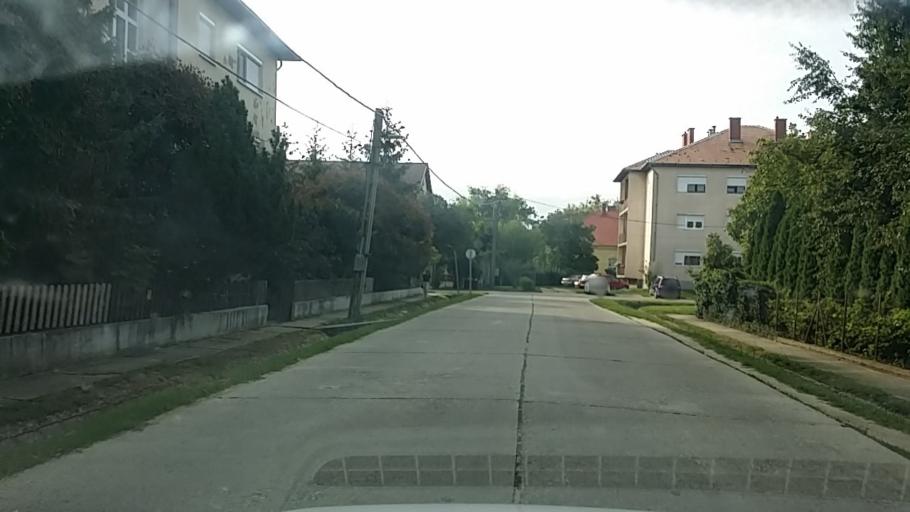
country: HU
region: Gyor-Moson-Sopron
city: Fertod
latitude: 47.6206
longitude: 16.8869
